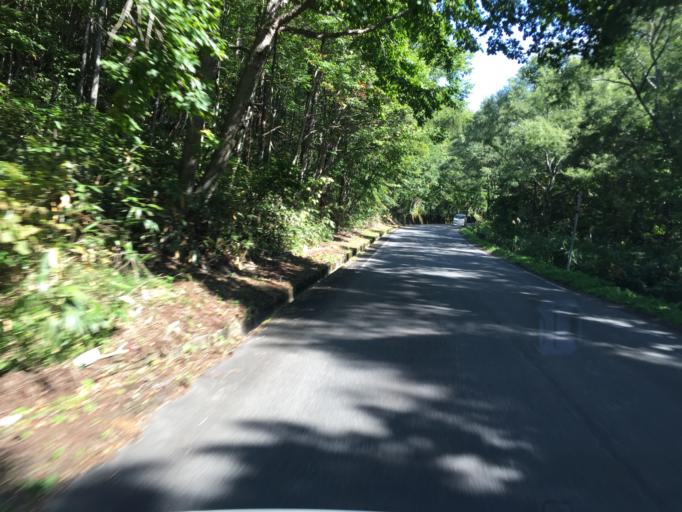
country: JP
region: Fukushima
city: Inawashiro
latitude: 37.6496
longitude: 140.2083
